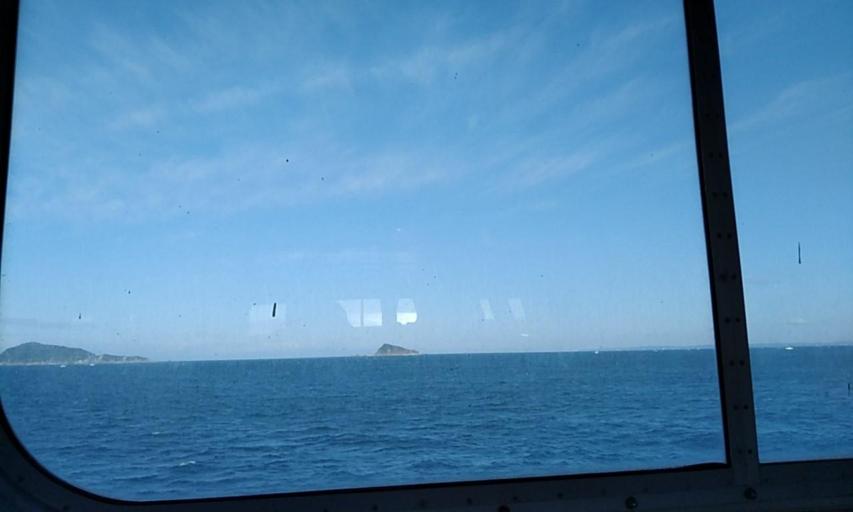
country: JP
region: Mie
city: Toba
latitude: 34.5288
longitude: 136.9421
